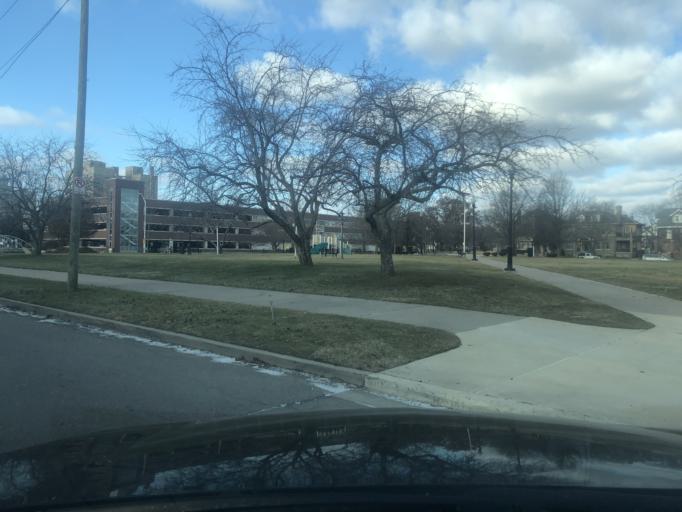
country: US
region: Michigan
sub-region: Wayne County
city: Hamtramck
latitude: 42.3614
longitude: -83.0602
